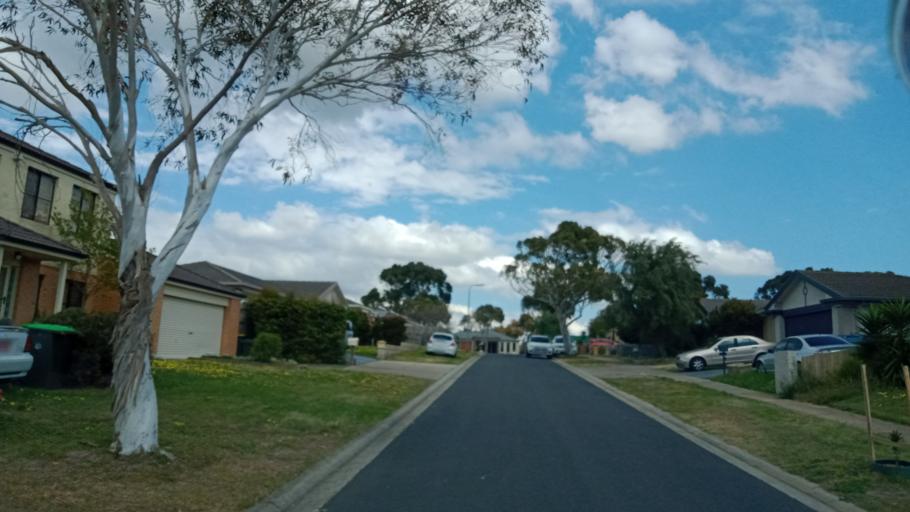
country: AU
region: Victoria
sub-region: Frankston
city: Sandhurst
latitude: -38.0933
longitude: 145.2021
